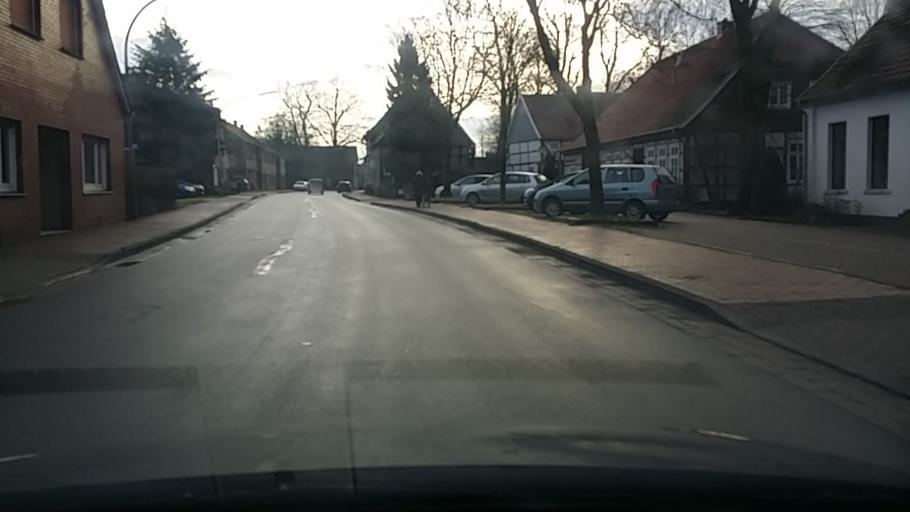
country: DE
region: Lower Saxony
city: Menslage
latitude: 52.6770
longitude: 7.8168
